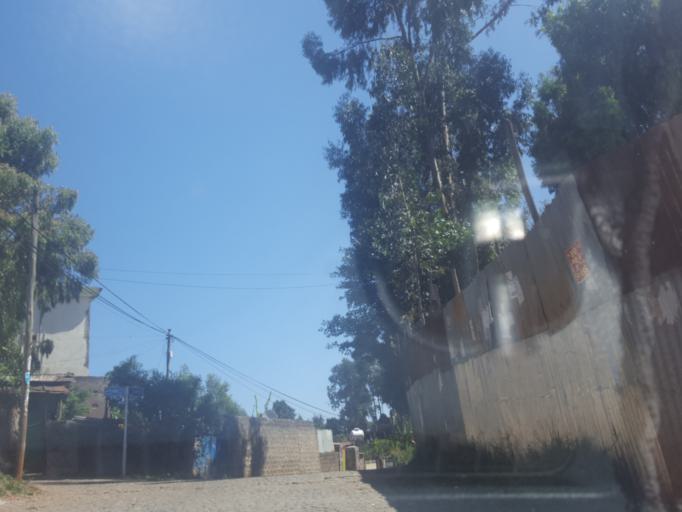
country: ET
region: Adis Abeba
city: Addis Ababa
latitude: 9.0621
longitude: 38.7386
